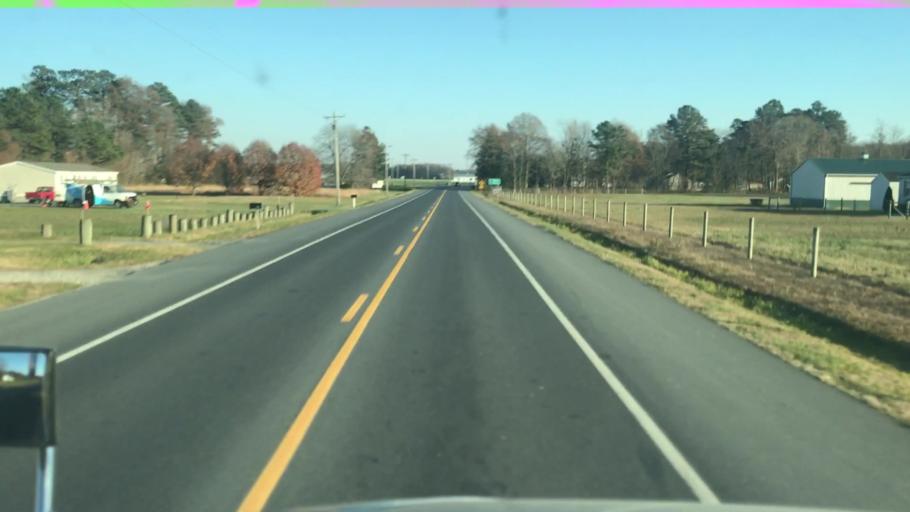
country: US
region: Delaware
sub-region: Sussex County
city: Bridgeville
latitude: 38.7828
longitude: -75.6723
